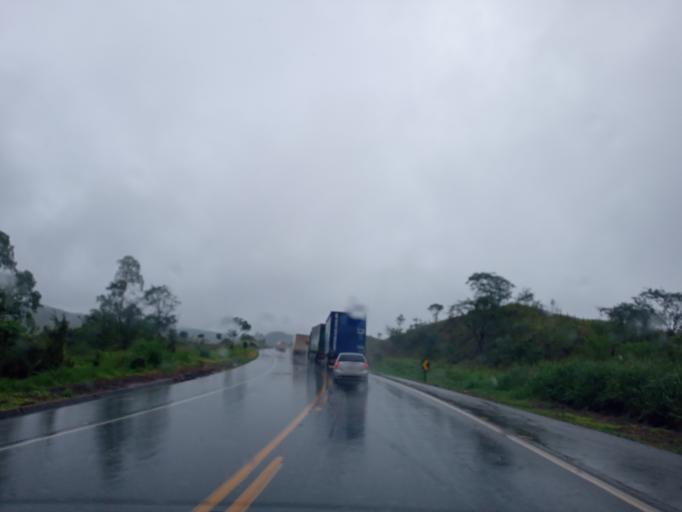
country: BR
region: Minas Gerais
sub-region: Luz
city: Luz
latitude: -19.7319
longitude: -45.8629
